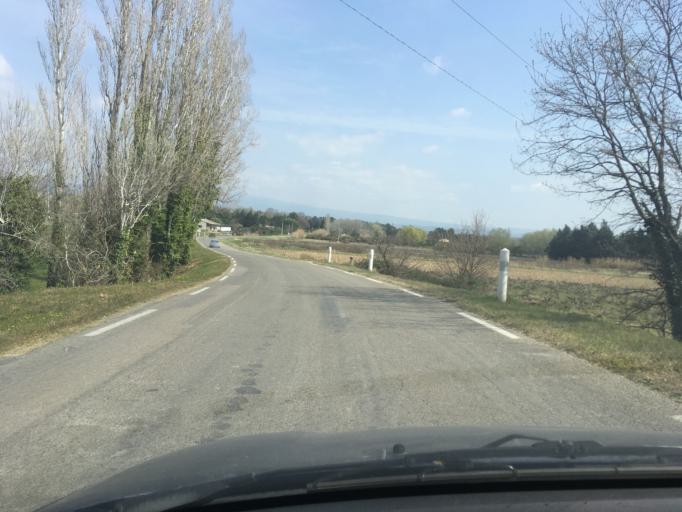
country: FR
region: Provence-Alpes-Cote d'Azur
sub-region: Departement du Vaucluse
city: Aubignan
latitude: 44.0999
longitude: 5.0012
